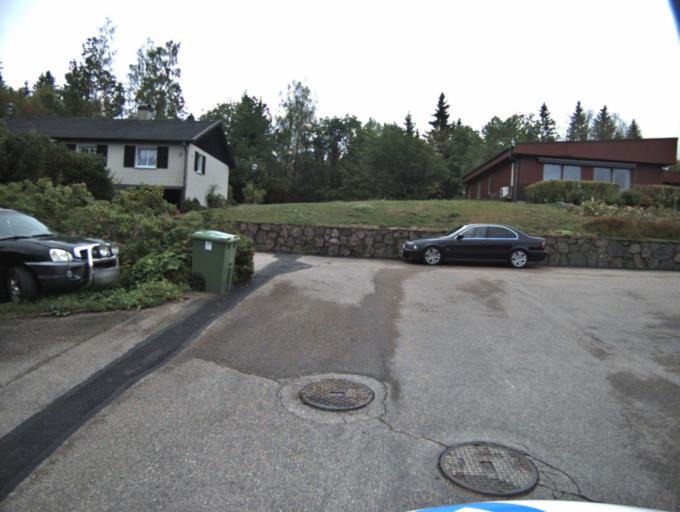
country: SE
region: Vaestra Goetaland
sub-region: Tranemo Kommun
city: Langhem
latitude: 57.7011
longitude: 13.3040
